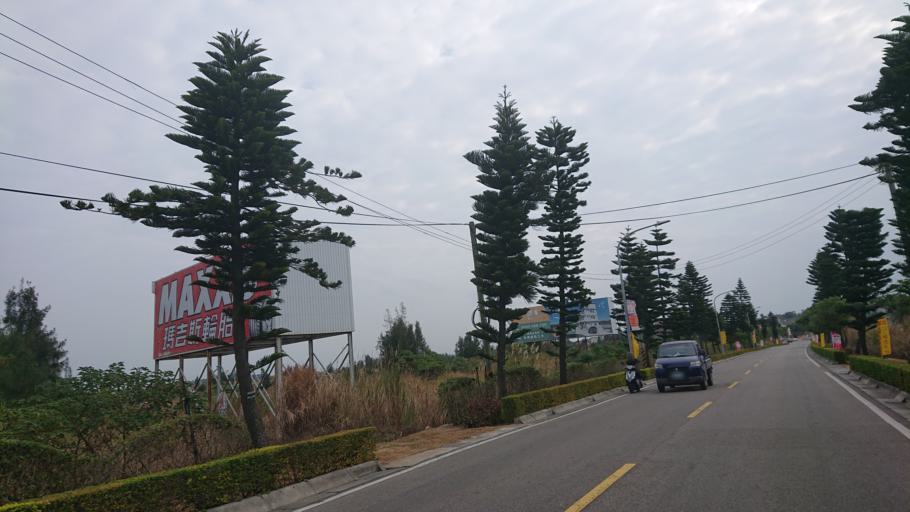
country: TW
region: Fukien
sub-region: Kinmen
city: Jincheng
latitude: 24.4124
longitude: 118.2910
